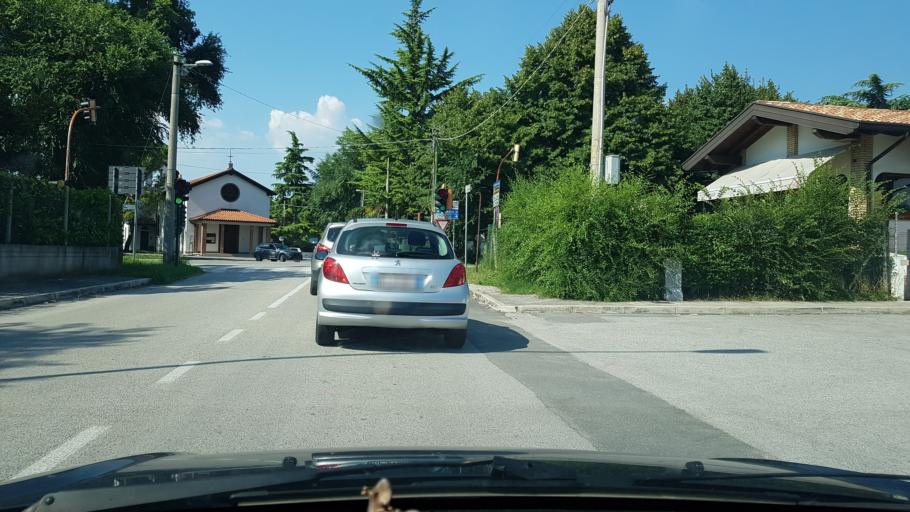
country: IT
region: Friuli Venezia Giulia
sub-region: Provincia di Gorizia
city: Staranzano
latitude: 45.7941
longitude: 13.5034
